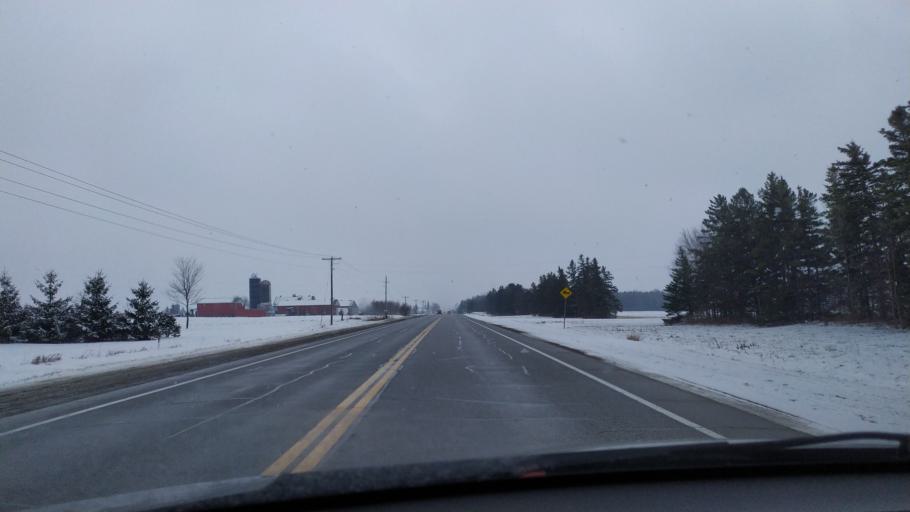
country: CA
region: Ontario
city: Waterloo
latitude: 43.6276
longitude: -80.7044
